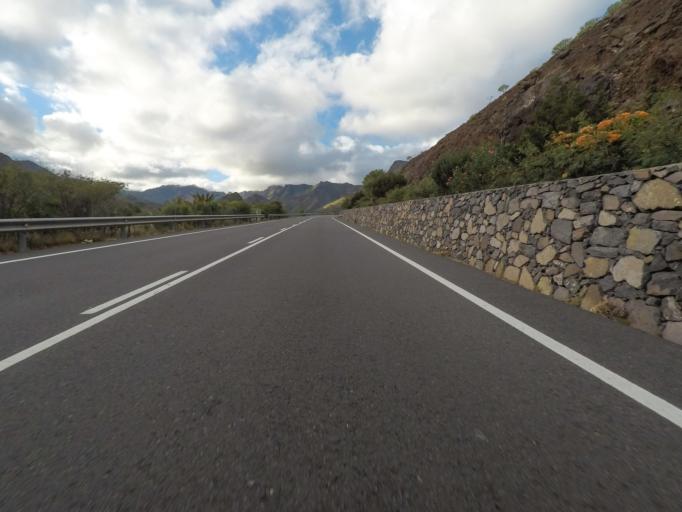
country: ES
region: Canary Islands
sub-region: Provincia de Santa Cruz de Tenerife
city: San Sebastian de la Gomera
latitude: 28.1027
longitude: -17.1219
